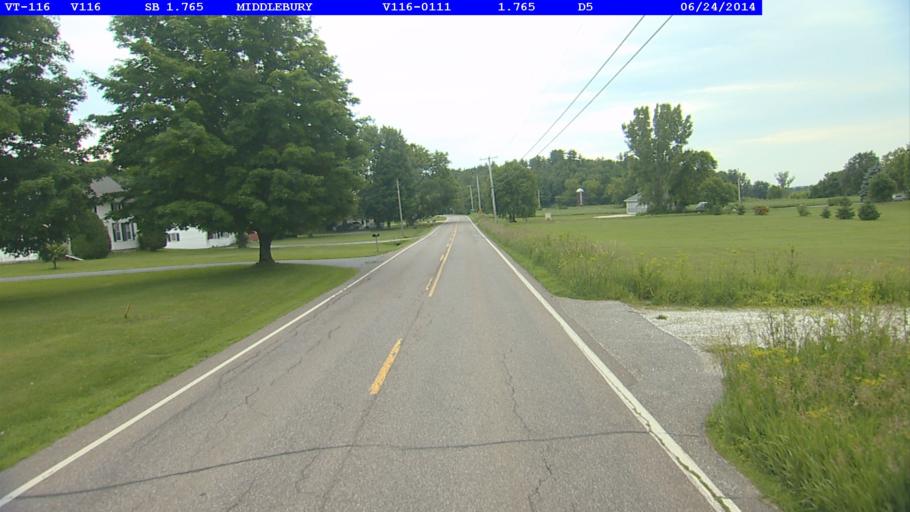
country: US
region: Vermont
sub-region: Addison County
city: Middlebury (village)
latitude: 43.9900
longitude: -73.1049
